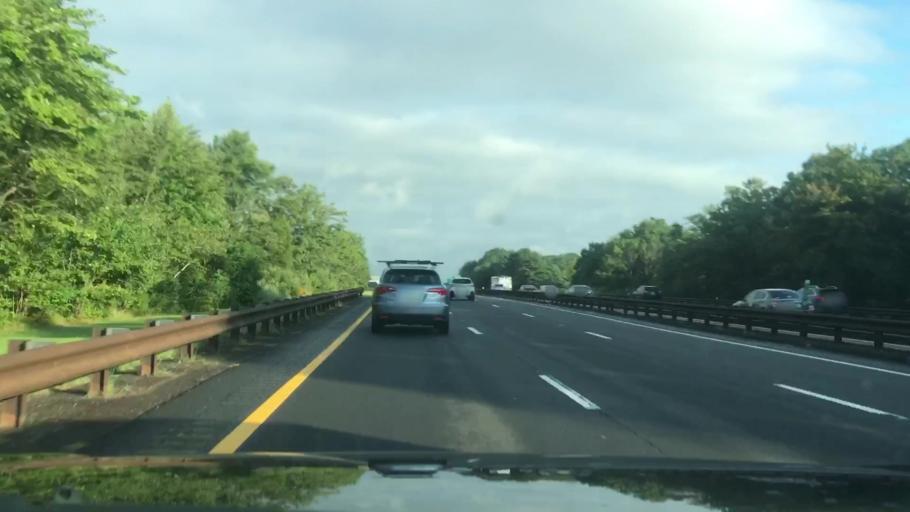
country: US
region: New Jersey
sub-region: Middlesex County
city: Laurence Harbor
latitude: 40.4326
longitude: -74.2478
